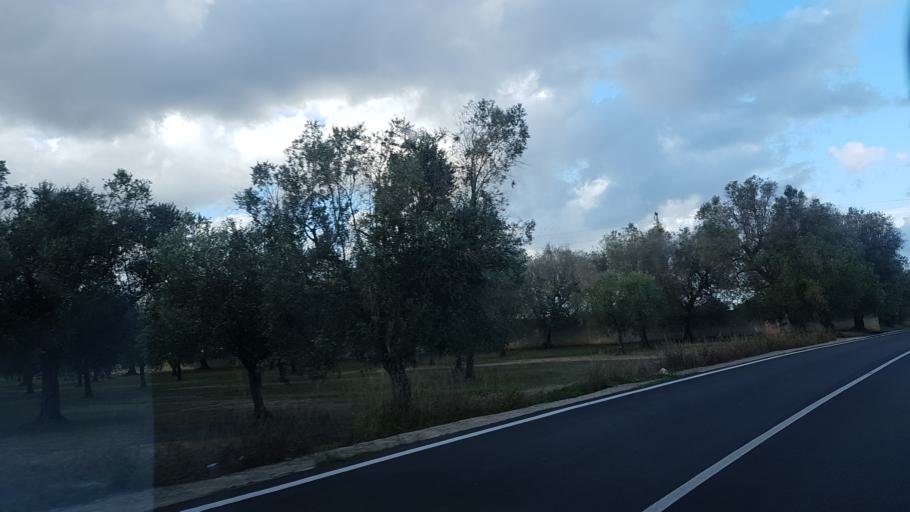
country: IT
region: Apulia
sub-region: Provincia di Brindisi
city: San Pietro Vernotico
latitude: 40.5073
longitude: 18.0082
